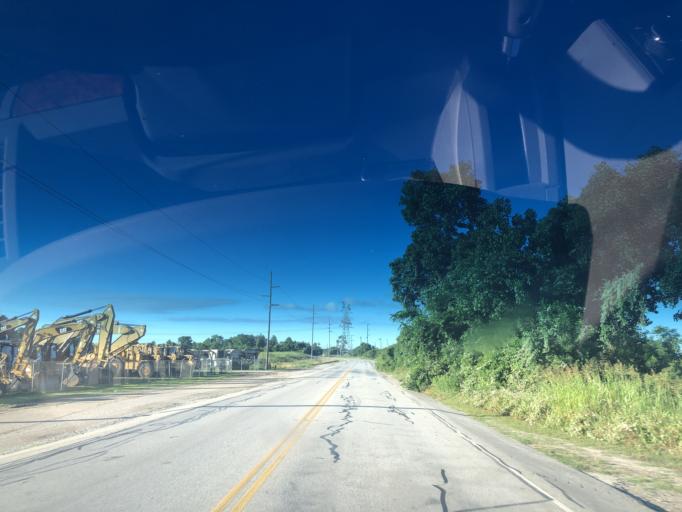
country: US
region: Texas
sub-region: Dallas County
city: Grand Prairie
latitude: 32.7883
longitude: -97.0172
